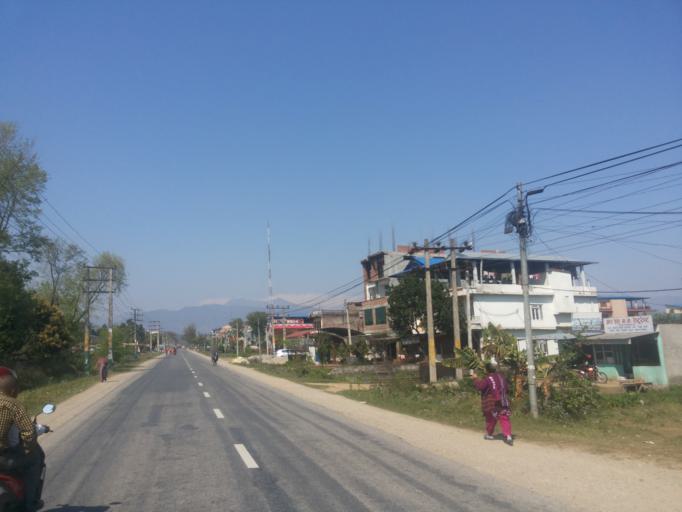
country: NP
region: Central Region
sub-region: Narayani Zone
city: Bharatpur
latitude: 27.6824
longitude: 84.4395
